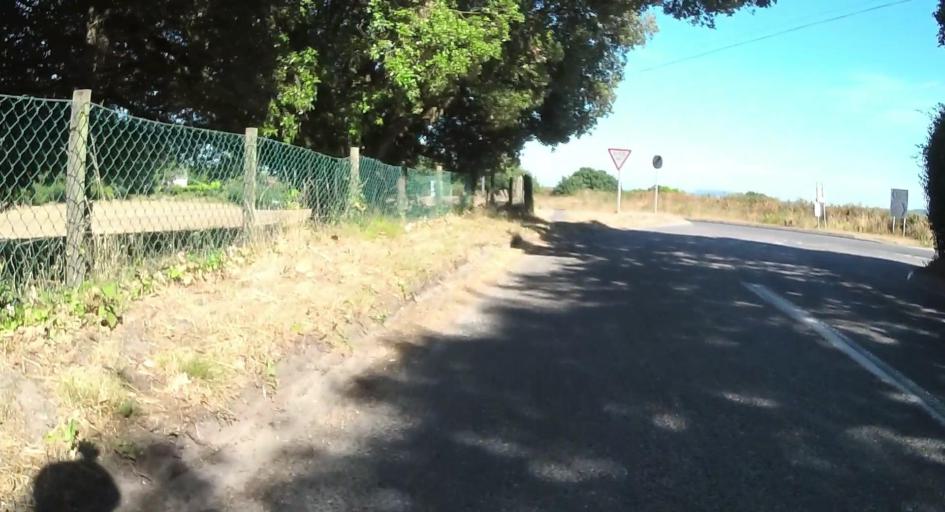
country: GB
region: England
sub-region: Dorset
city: Wareham
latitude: 50.6830
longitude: -2.1374
